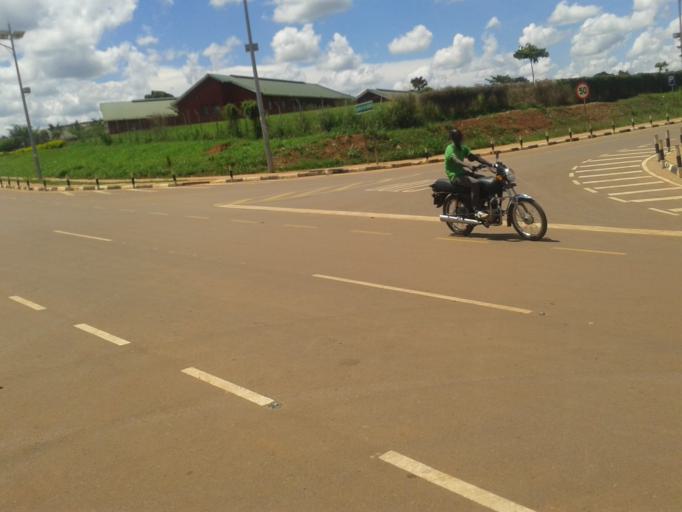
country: UG
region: Northern Region
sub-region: Gulu District
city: Gulu
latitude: 2.7649
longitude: 32.2934
